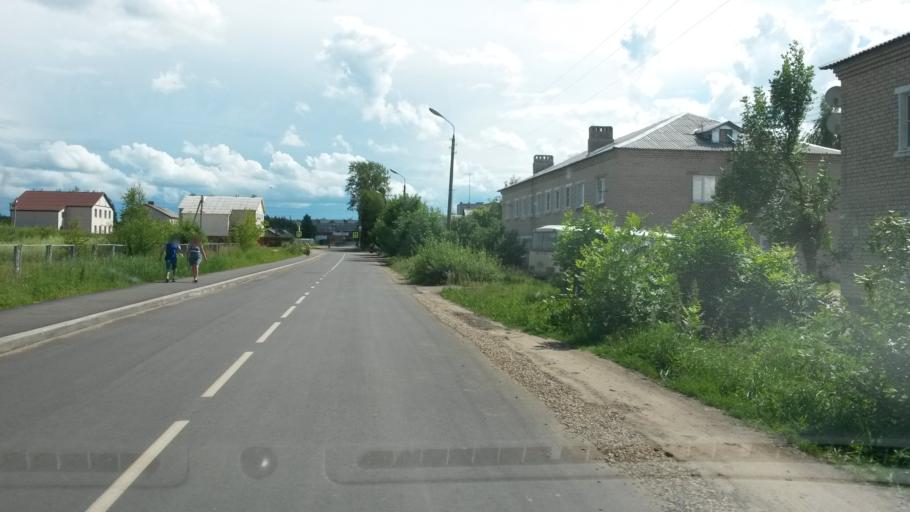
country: RU
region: Jaroslavl
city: Gavrilov-Yam
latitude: 57.3102
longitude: 39.8658
